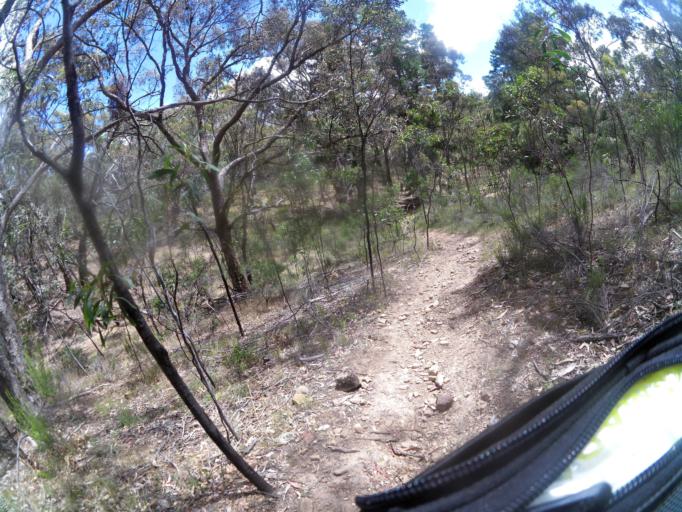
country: AU
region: Victoria
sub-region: Mount Alexander
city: Castlemaine
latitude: -37.0607
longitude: 144.2665
